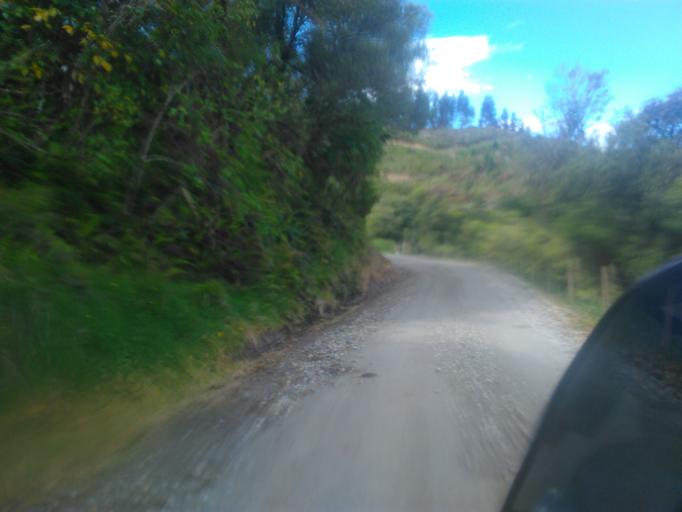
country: NZ
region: Hawke's Bay
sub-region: Wairoa District
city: Wairoa
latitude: -38.7760
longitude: 177.6255
